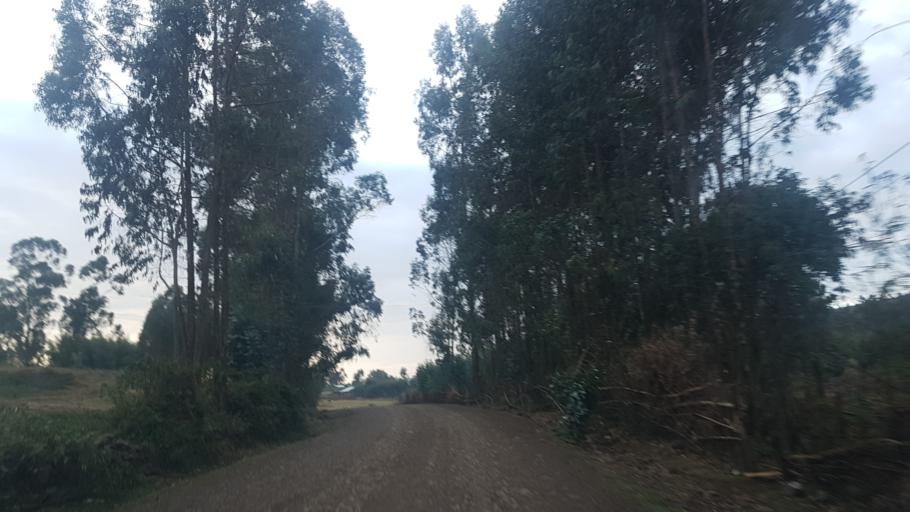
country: ET
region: Amhara
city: Finote Selam
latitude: 10.8105
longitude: 37.6535
